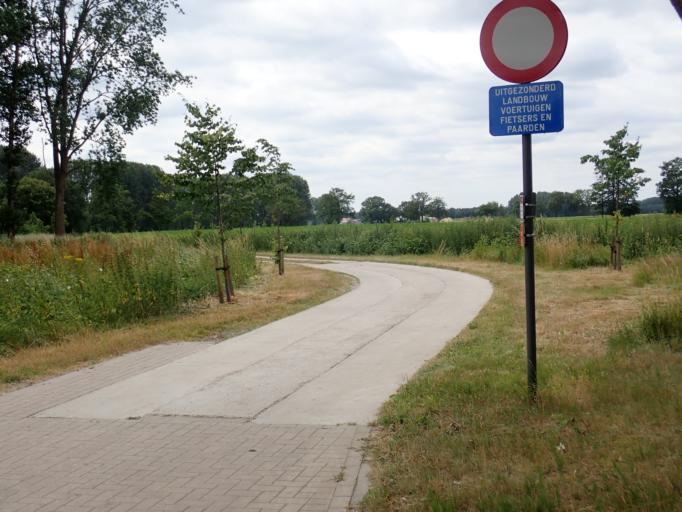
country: BE
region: Flanders
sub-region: Provincie Antwerpen
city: Baarle-Hertog
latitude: 51.4019
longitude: 4.8882
